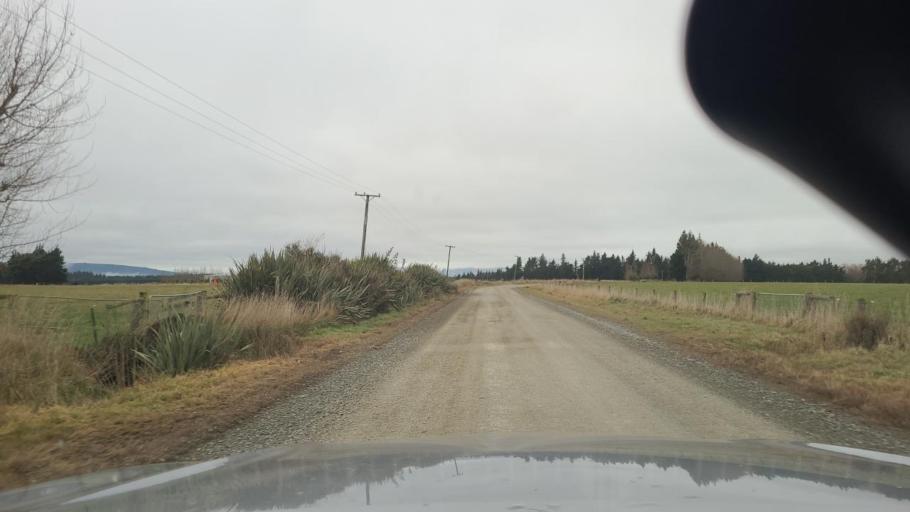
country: NZ
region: Southland
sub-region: Southland District
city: Te Anau
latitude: -45.6608
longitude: 168.1498
